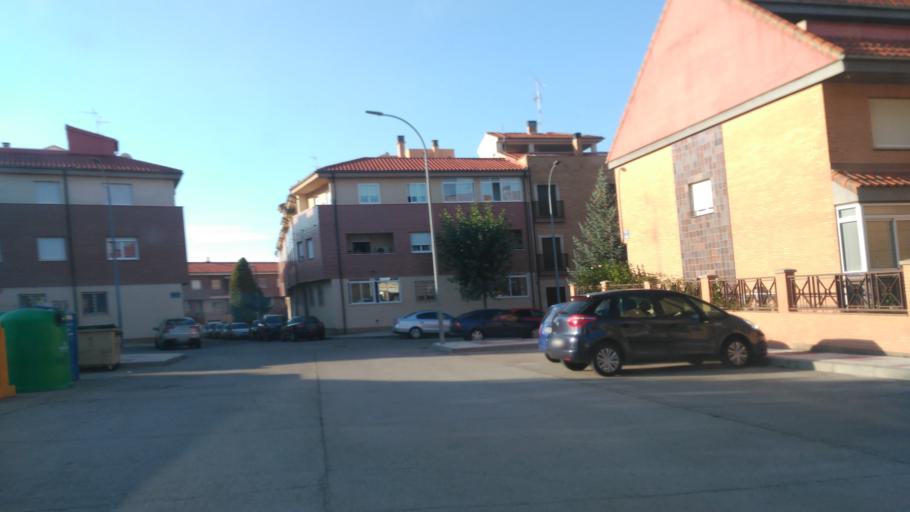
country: ES
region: Castille and Leon
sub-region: Provincia de Salamanca
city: Carbajosa de la Sagrada
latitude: 40.9307
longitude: -5.6507
